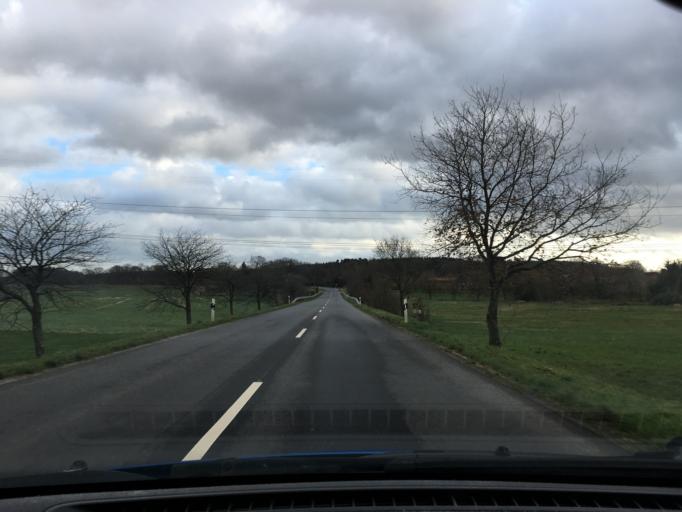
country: DE
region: Schleswig-Holstein
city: Kaaks
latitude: 53.9891
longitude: 9.4754
